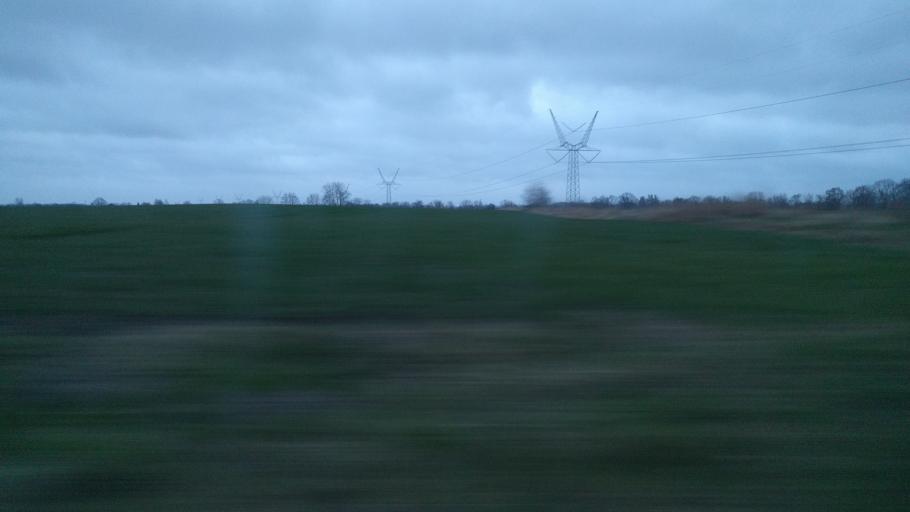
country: DK
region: South Denmark
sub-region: Odense Kommune
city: Bullerup
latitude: 55.3969
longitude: 10.5068
